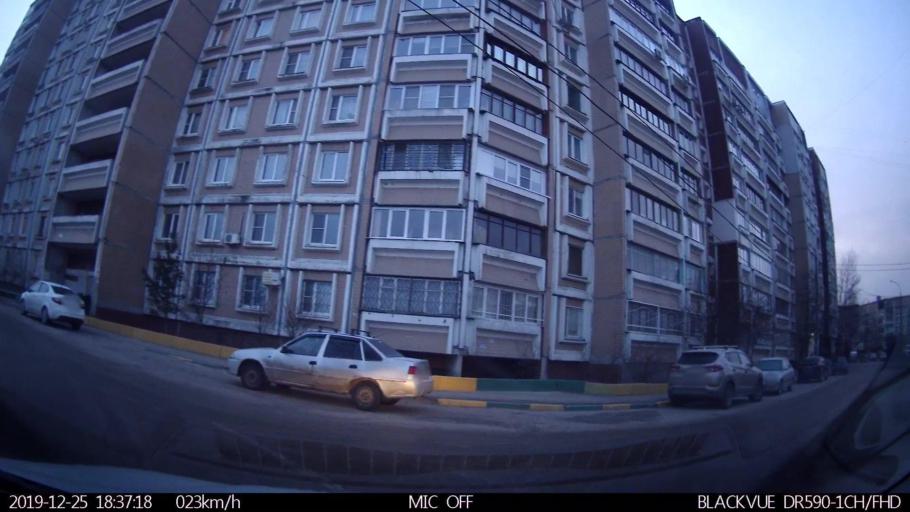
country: RU
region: Nizjnij Novgorod
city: Nizhniy Novgorod
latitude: 56.3456
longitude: 43.9395
